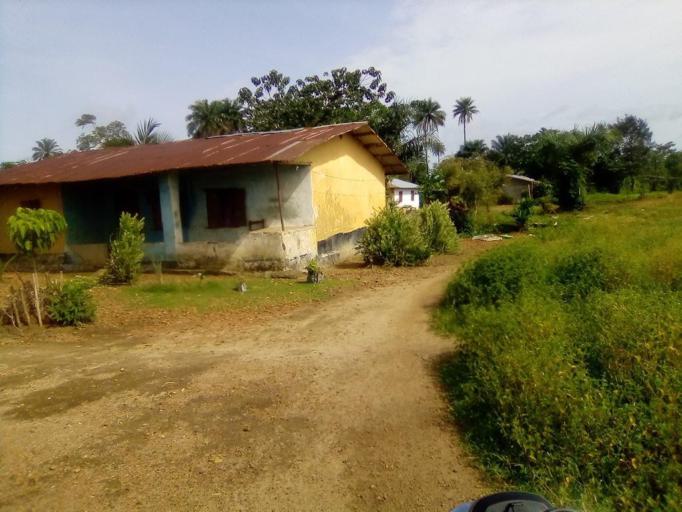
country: SL
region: Southern Province
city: Pujehun
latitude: 7.3649
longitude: -11.7284
